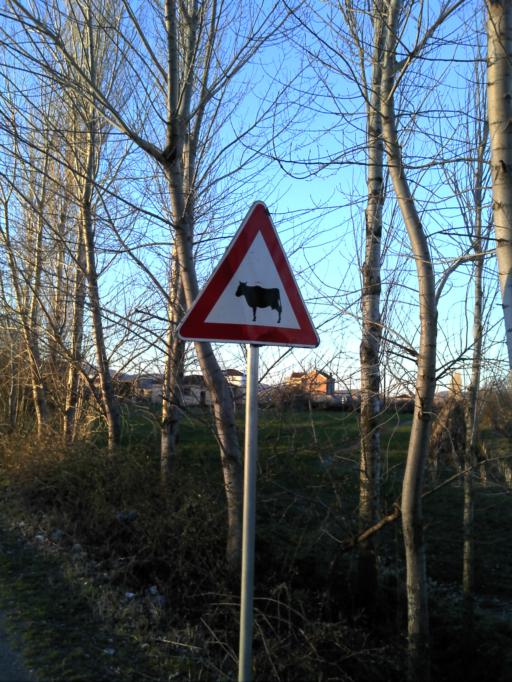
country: AL
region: Shkoder
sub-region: Rrethi i Shkodres
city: Berdica e Madhe
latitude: 41.9851
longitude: 19.4804
